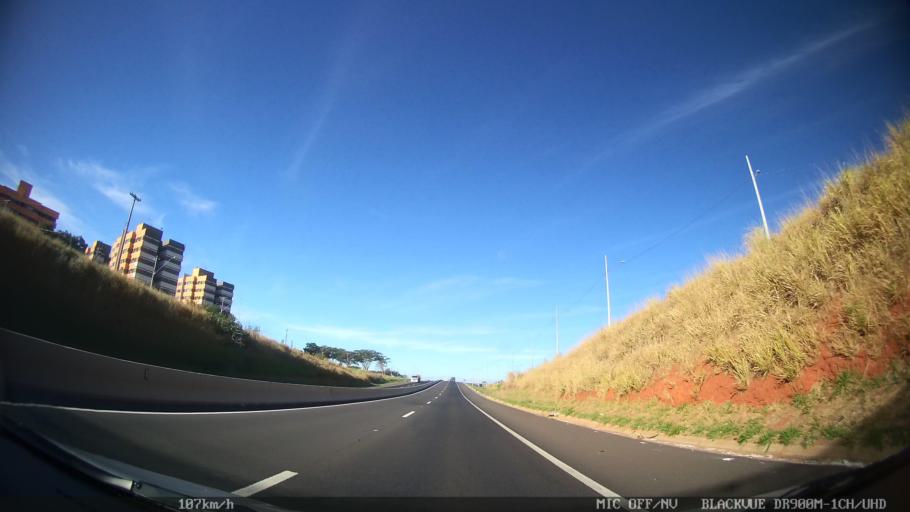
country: BR
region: Sao Paulo
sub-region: Sao Jose Do Rio Preto
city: Sao Jose do Rio Preto
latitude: -20.8503
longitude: -49.3925
